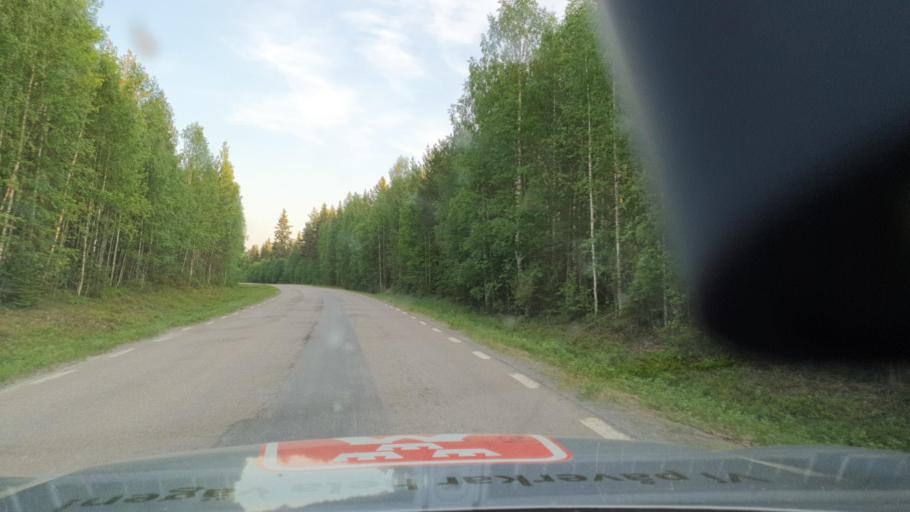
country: SE
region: Norrbotten
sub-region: Bodens Kommun
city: Boden
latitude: 66.0509
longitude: 21.7848
